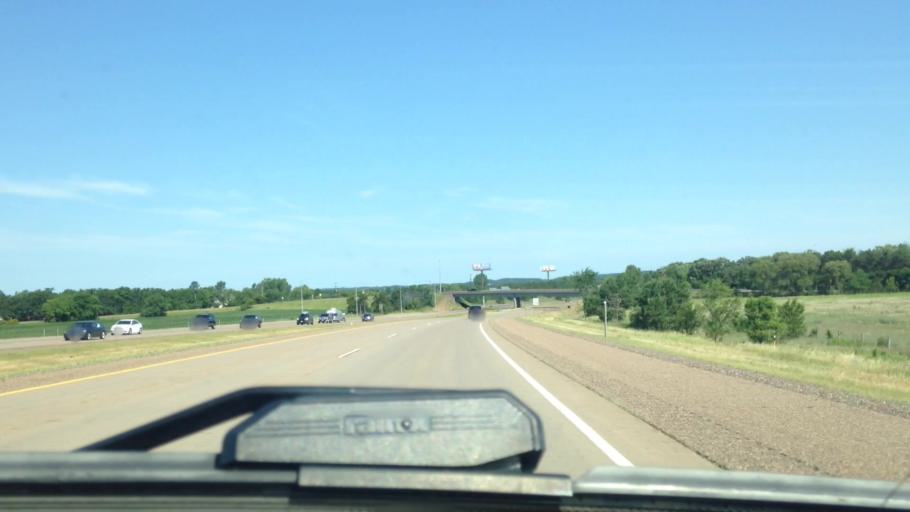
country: US
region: Wisconsin
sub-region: Chippewa County
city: Lake Hallie
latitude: 44.8977
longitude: -91.4226
